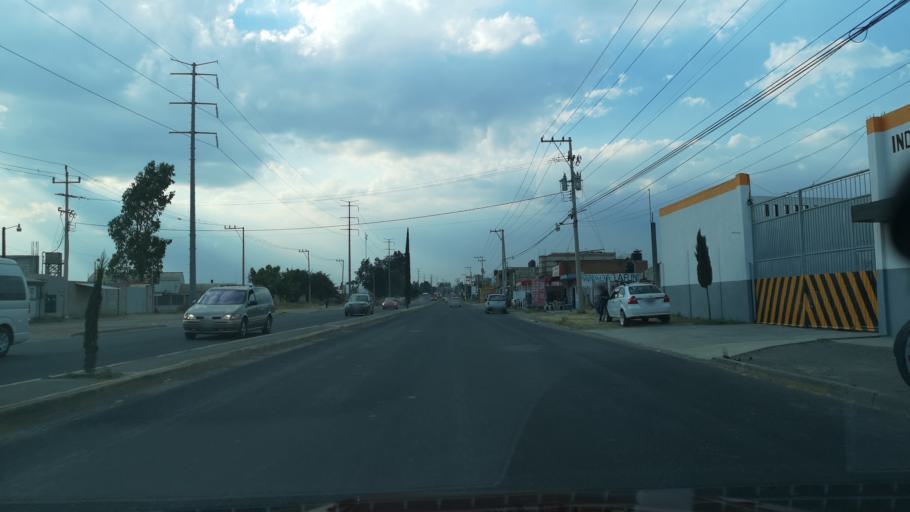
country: MX
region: Puebla
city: Cuanala
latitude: 19.0913
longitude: -98.3368
